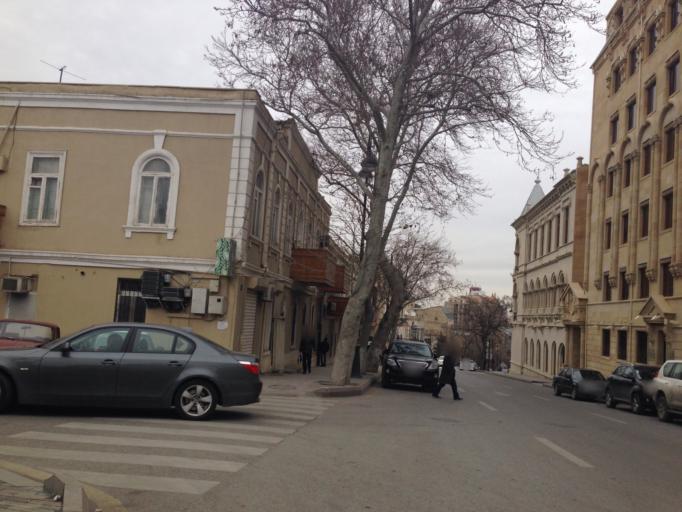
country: AZ
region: Baki
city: Badamdar
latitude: 40.3703
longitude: 49.8302
